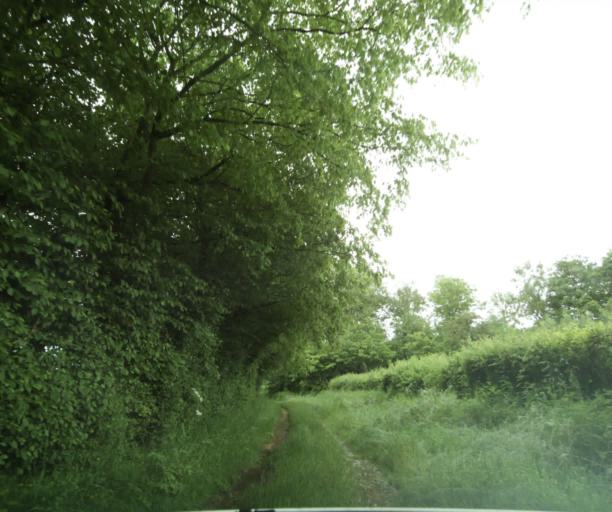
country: FR
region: Bourgogne
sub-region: Departement de Saone-et-Loire
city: Charolles
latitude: 46.4612
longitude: 4.3531
